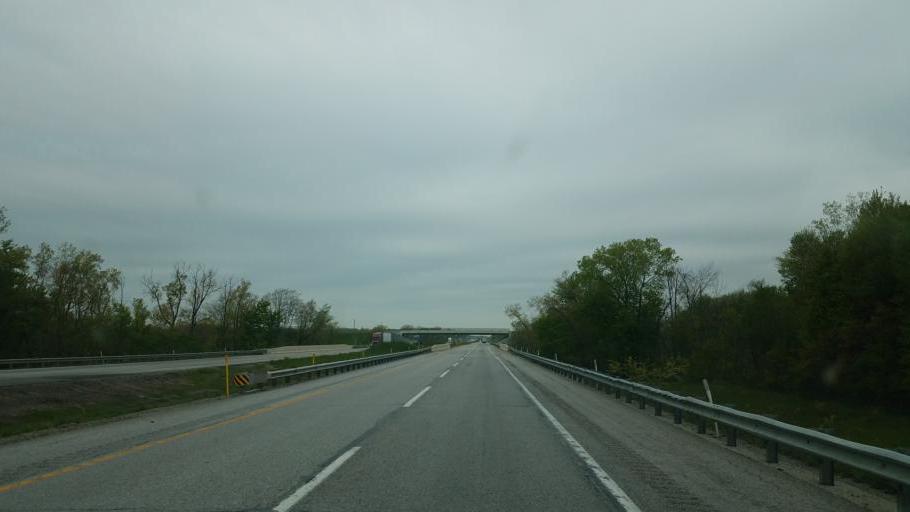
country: US
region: Michigan
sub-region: Saint Joseph County
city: White Pigeon
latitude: 41.7538
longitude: -85.5786
